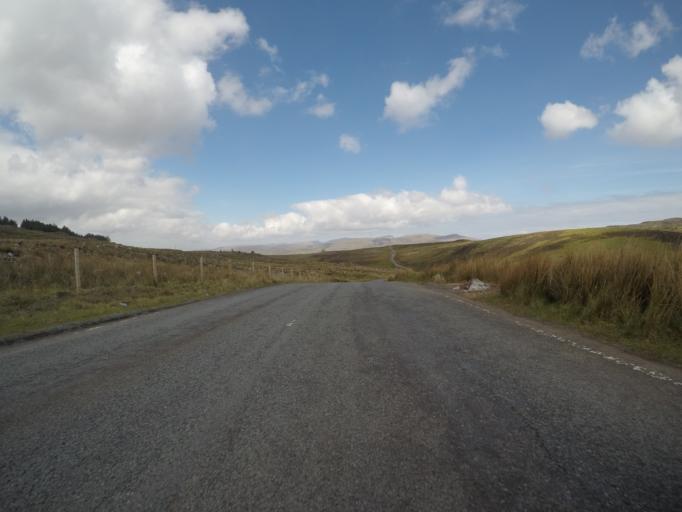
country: GB
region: Scotland
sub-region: Highland
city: Isle of Skye
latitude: 57.4127
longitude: -6.2997
